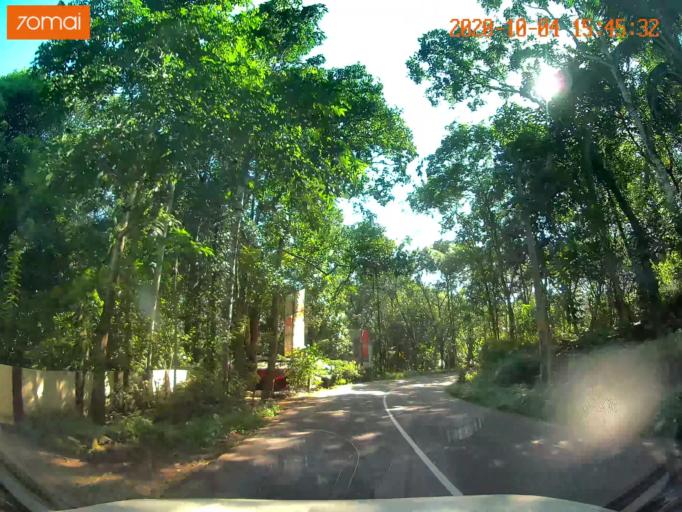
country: IN
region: Kerala
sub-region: Kottayam
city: Palackattumala
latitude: 9.7607
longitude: 76.5798
